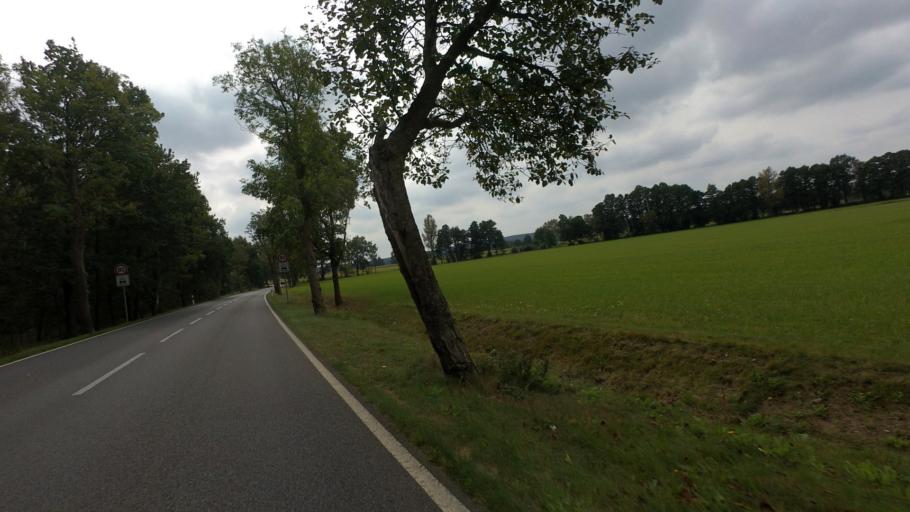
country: DE
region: Brandenburg
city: Luckau
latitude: 51.7857
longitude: 13.6886
